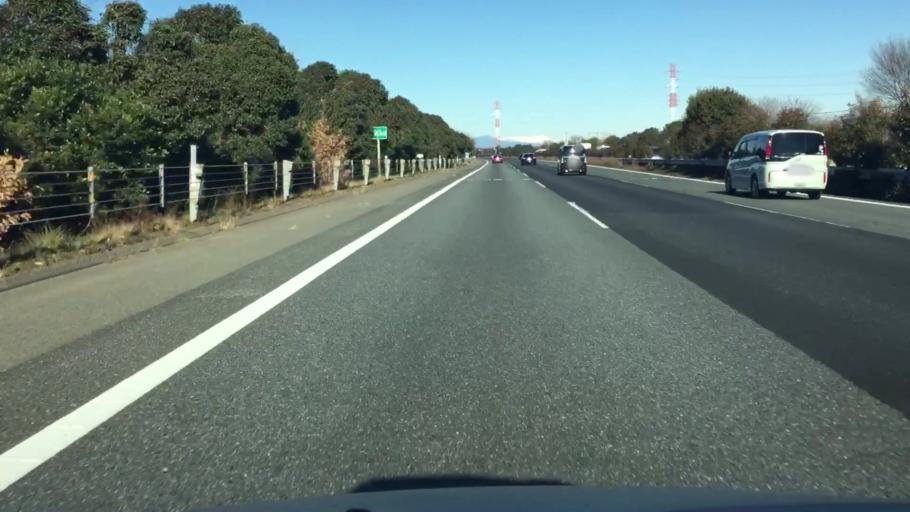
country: JP
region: Saitama
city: Yorii
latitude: 36.1449
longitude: 139.2230
